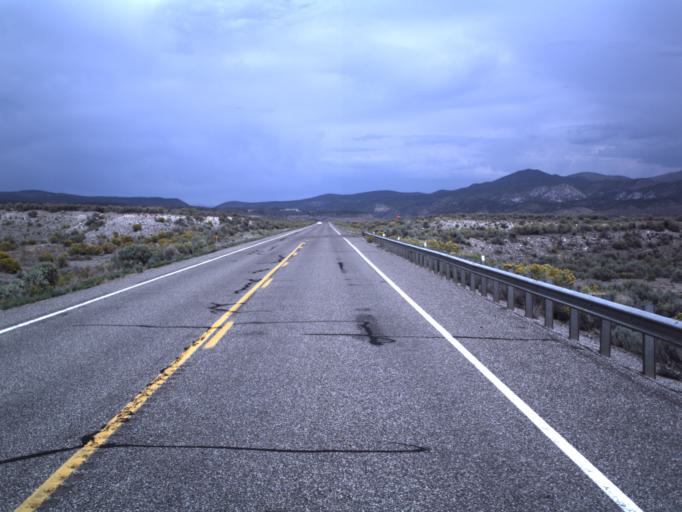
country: US
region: Utah
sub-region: Garfield County
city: Panguitch
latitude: 37.9820
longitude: -112.3999
